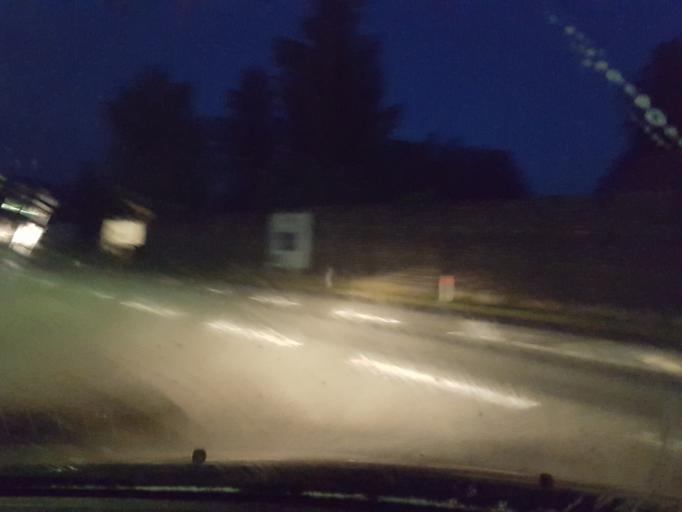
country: AT
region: Lower Austria
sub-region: Politischer Bezirk Scheibbs
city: Purgstall
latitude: 48.0619
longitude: 15.1392
